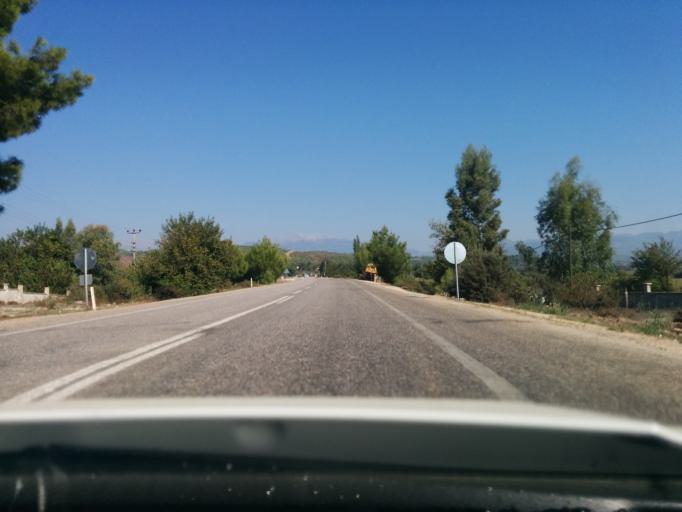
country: TR
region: Mugla
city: Kemer
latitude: 36.5867
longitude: 29.3504
